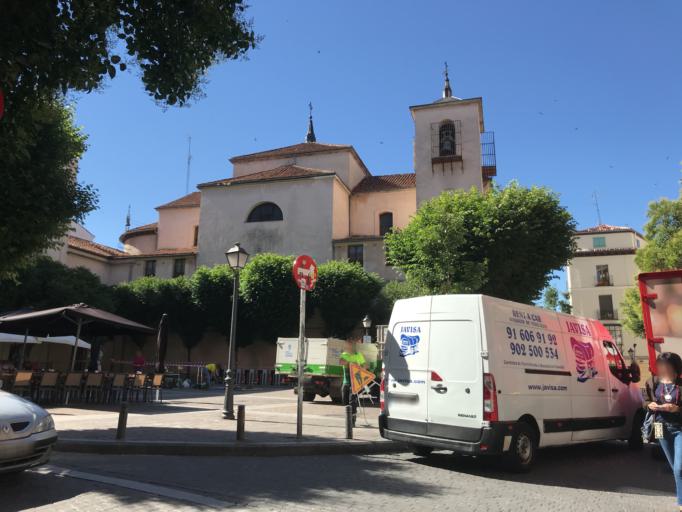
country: ES
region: Madrid
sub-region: Provincia de Madrid
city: City Center
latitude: 40.4244
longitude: -3.7021
